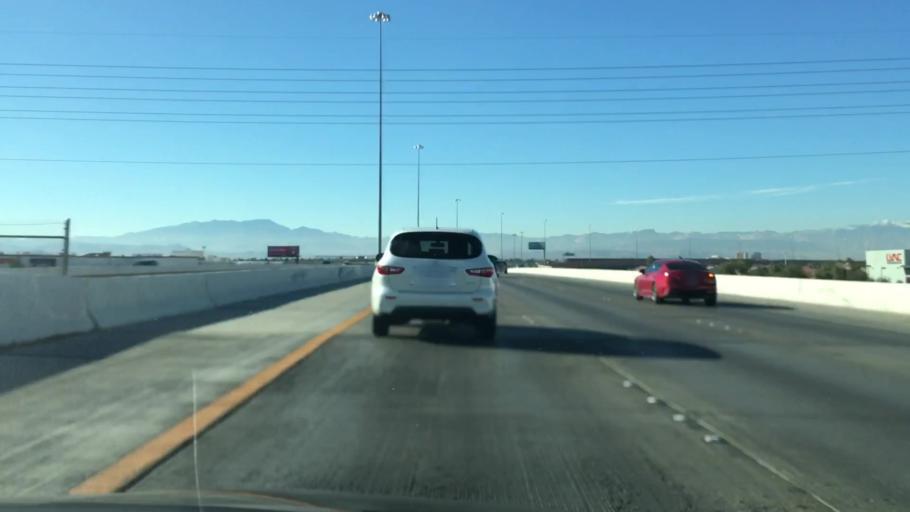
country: US
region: Nevada
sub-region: Clark County
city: Whitney
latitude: 36.0238
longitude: -115.1181
